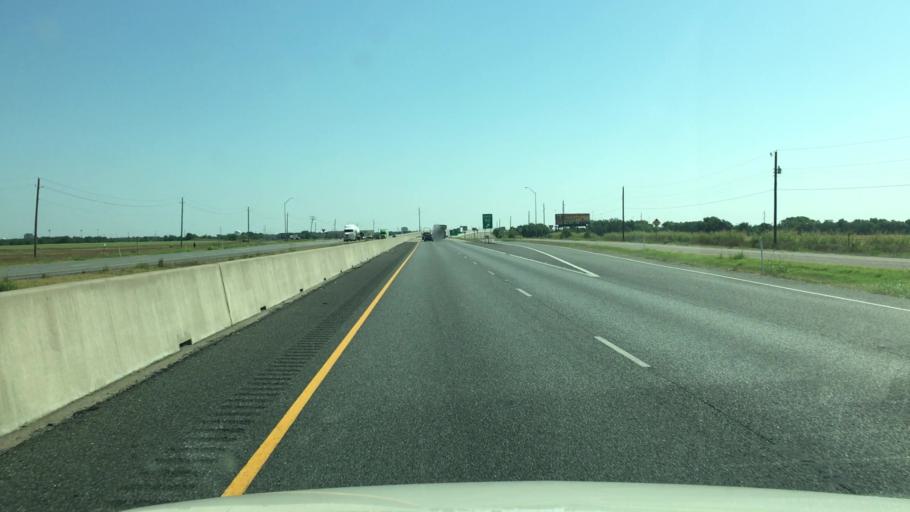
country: US
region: Texas
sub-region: Hunt County
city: Greenville
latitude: 33.0829
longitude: -96.1324
